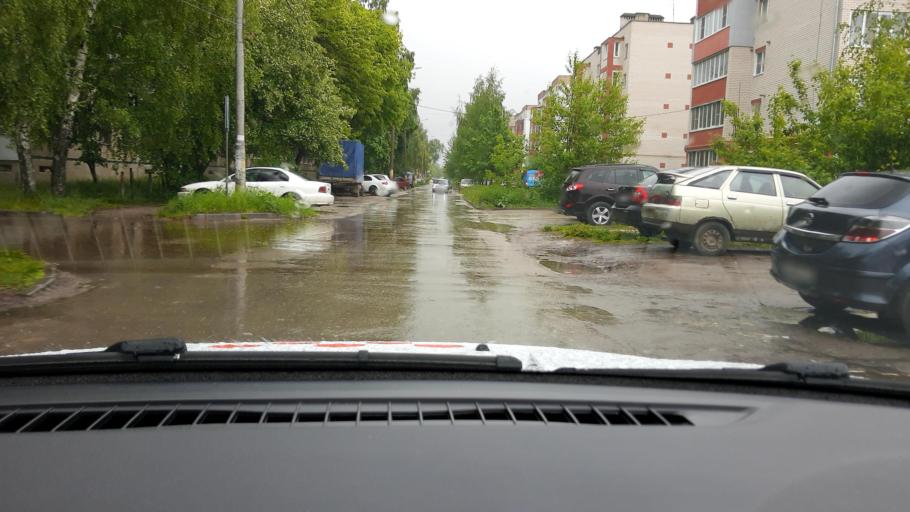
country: RU
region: Nizjnij Novgorod
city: Kstovo
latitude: 56.1387
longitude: 44.1892
